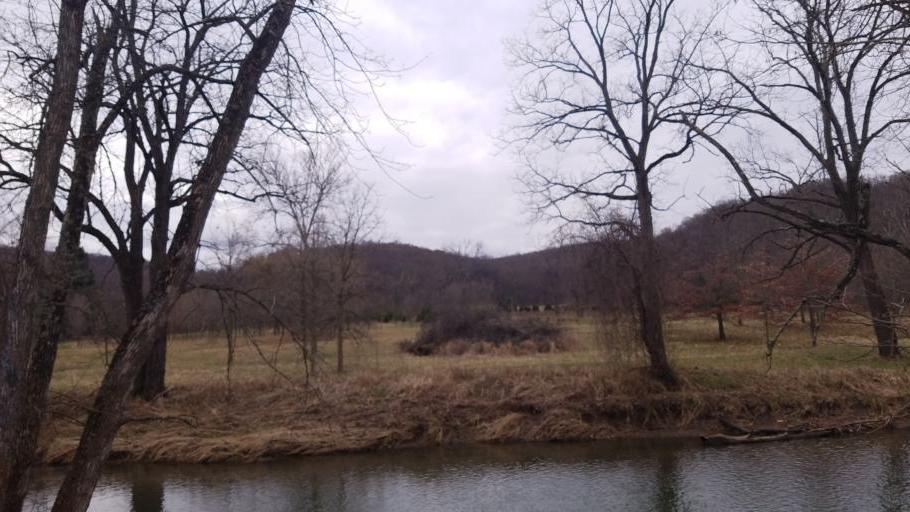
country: US
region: Ohio
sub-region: Sandusky County
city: Bellville
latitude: 40.6015
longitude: -82.4701
